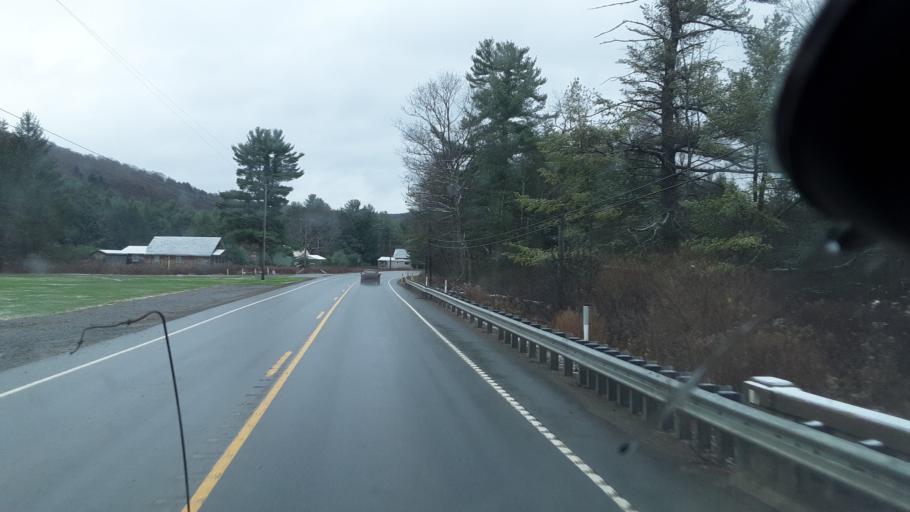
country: US
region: Pennsylvania
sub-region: Potter County
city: Shinglehouse
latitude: 41.9198
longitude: -78.1127
